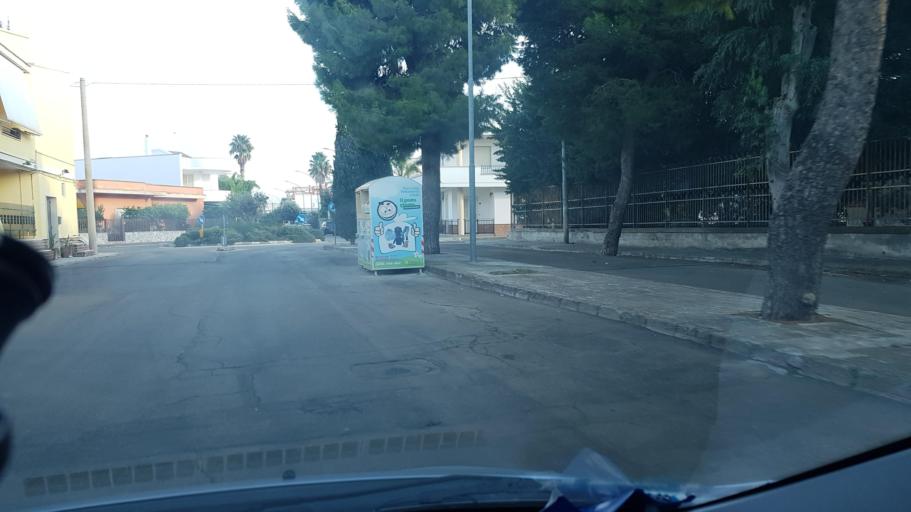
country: IT
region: Apulia
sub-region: Provincia di Lecce
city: Veglie
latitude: 40.3414
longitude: 17.9646
